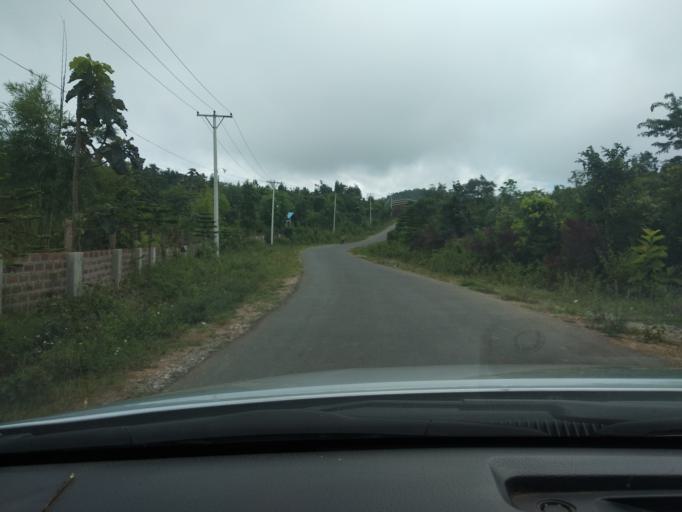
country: MM
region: Mandalay
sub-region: Pyin Oo Lwin District
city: Pyin Oo Lwin
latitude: 21.9211
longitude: 96.3785
